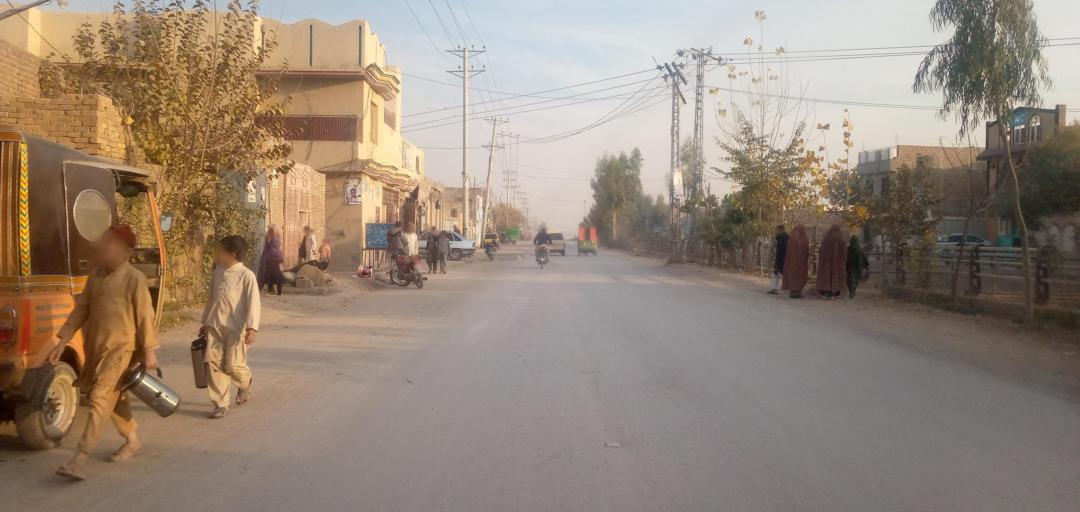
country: PK
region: Khyber Pakhtunkhwa
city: Peshawar
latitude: 33.9719
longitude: 71.5326
